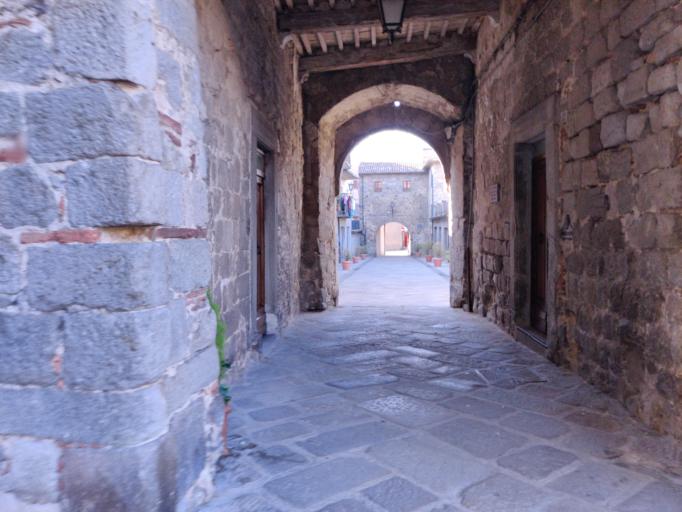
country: IT
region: Tuscany
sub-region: Provincia di Siena
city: Abbadia San Salvatore
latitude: 42.8822
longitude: 11.6761
